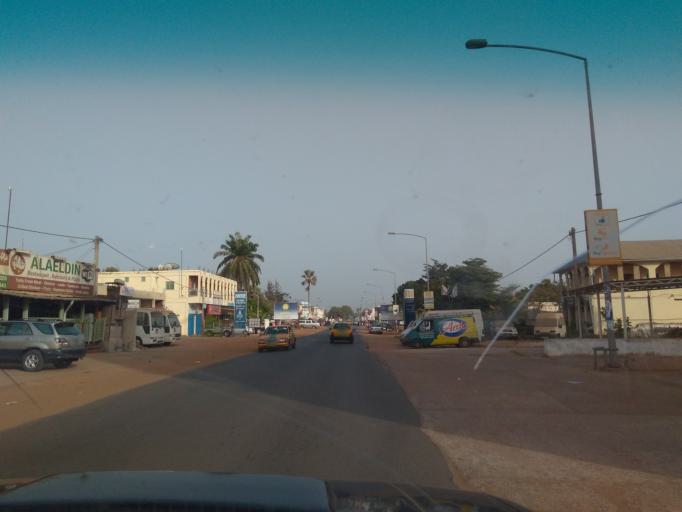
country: GM
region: Banjul
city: Bakau
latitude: 13.4662
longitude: -16.6902
